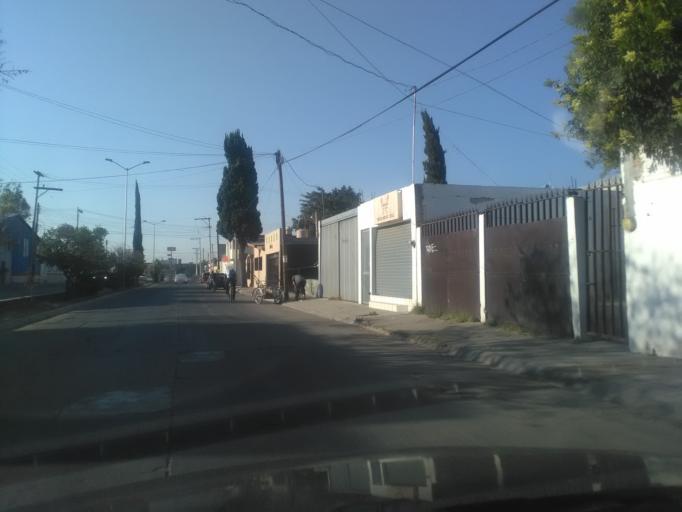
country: MX
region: Durango
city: Victoria de Durango
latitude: 24.0418
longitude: -104.6211
